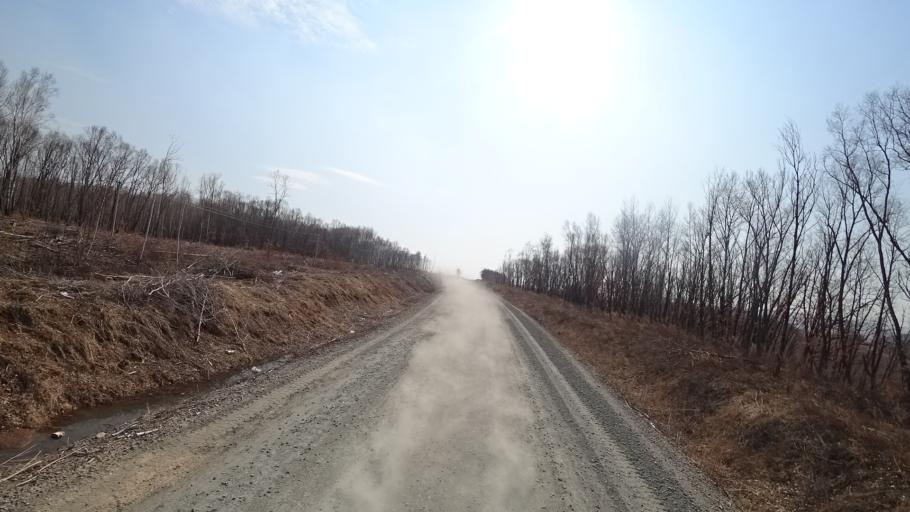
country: RU
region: Amur
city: Novobureyskiy
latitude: 49.8223
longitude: 129.9838
